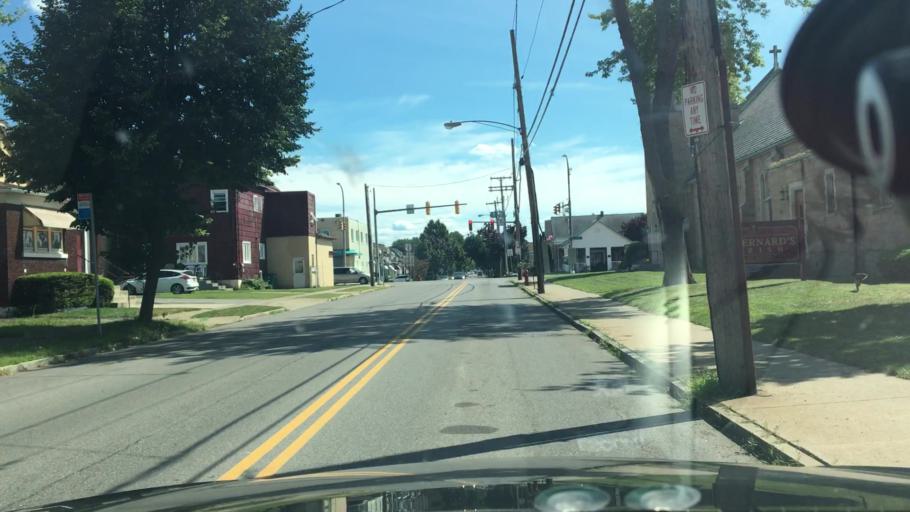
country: US
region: New York
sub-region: Erie County
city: Sloan
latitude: 42.8725
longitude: -78.8021
